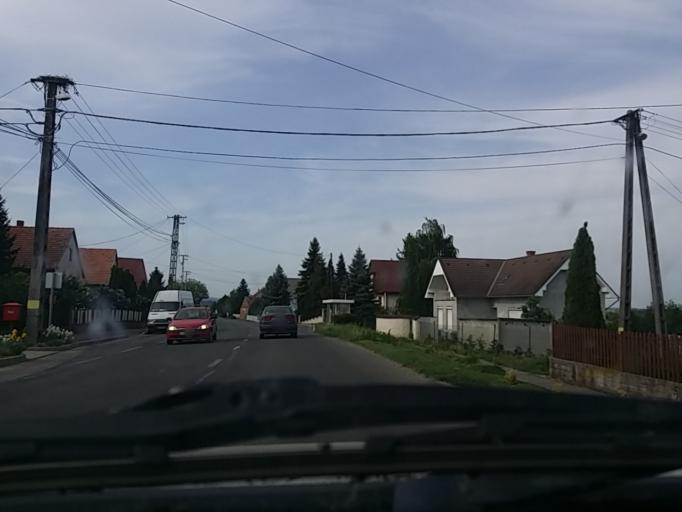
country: HU
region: Baranya
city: Harkany
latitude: 45.9410
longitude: 18.2378
